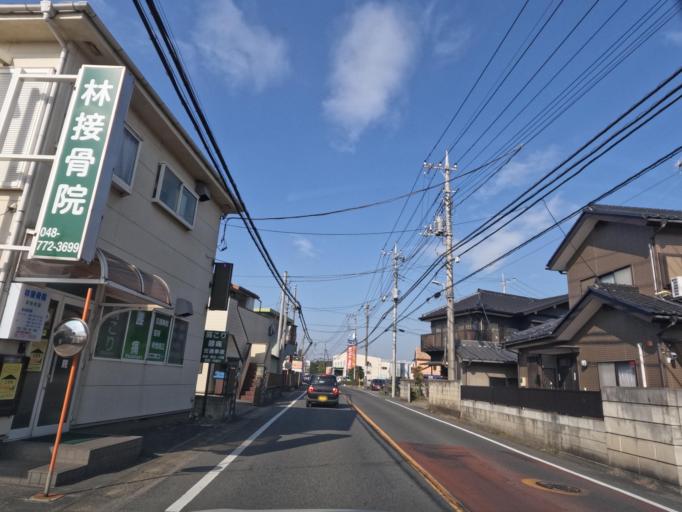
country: JP
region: Saitama
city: Ageoshimo
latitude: 35.9798
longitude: 139.6113
